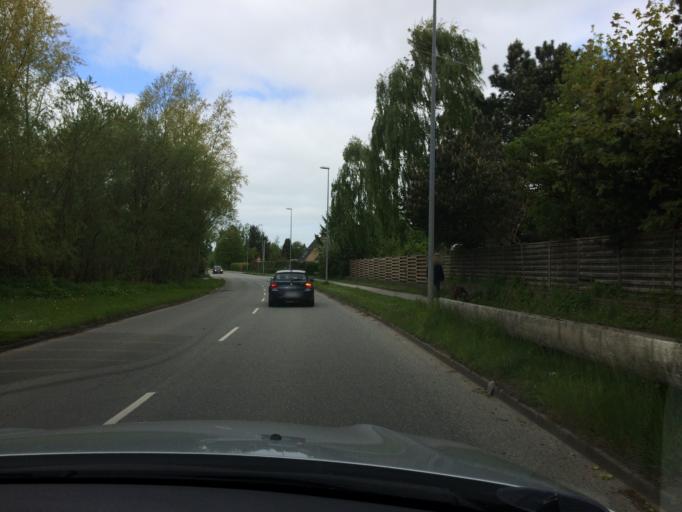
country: DK
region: Central Jutland
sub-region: Arhus Kommune
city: Hjortshoj
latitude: 56.2303
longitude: 10.2989
